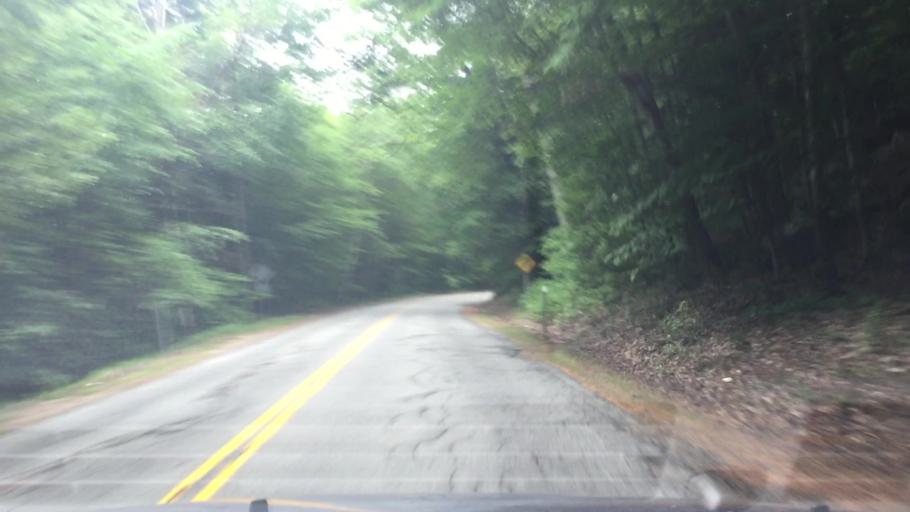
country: US
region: New Hampshire
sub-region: Carroll County
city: North Conway
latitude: 44.1012
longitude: -71.1748
